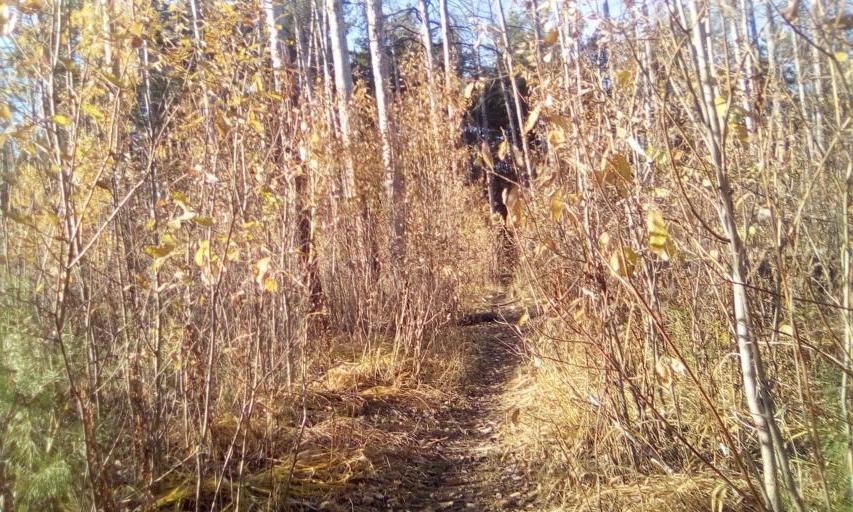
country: RU
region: Chelyabinsk
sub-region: Gorod Chelyabinsk
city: Chelyabinsk
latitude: 55.1628
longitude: 61.3546
